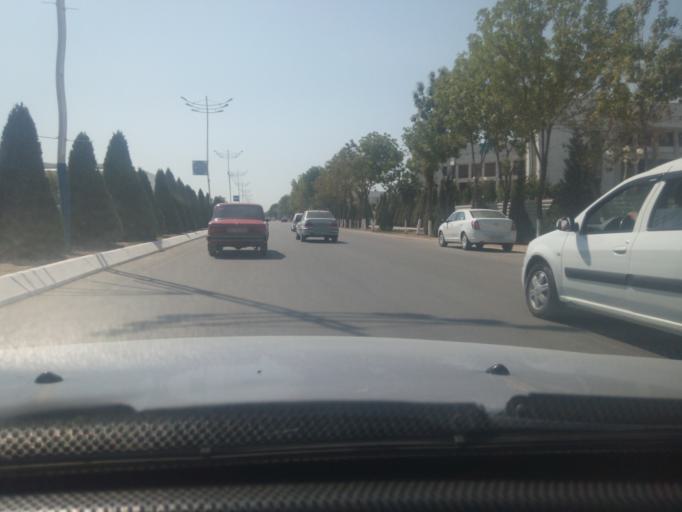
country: UZ
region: Sirdaryo
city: Guliston
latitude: 40.4986
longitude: 68.7744
